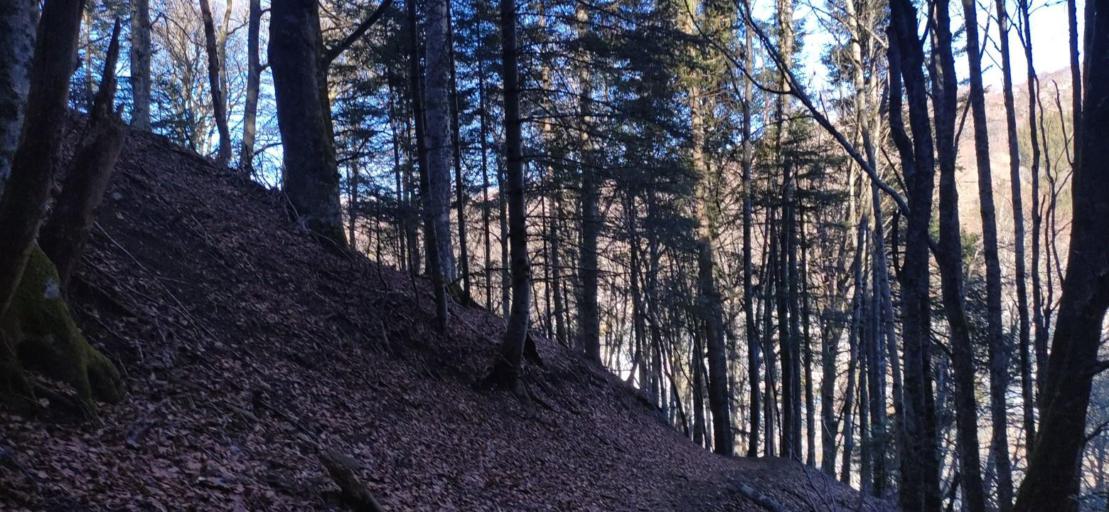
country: FR
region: Auvergne
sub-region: Departement du Puy-de-Dome
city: Mont-Dore
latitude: 45.5712
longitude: 2.8062
